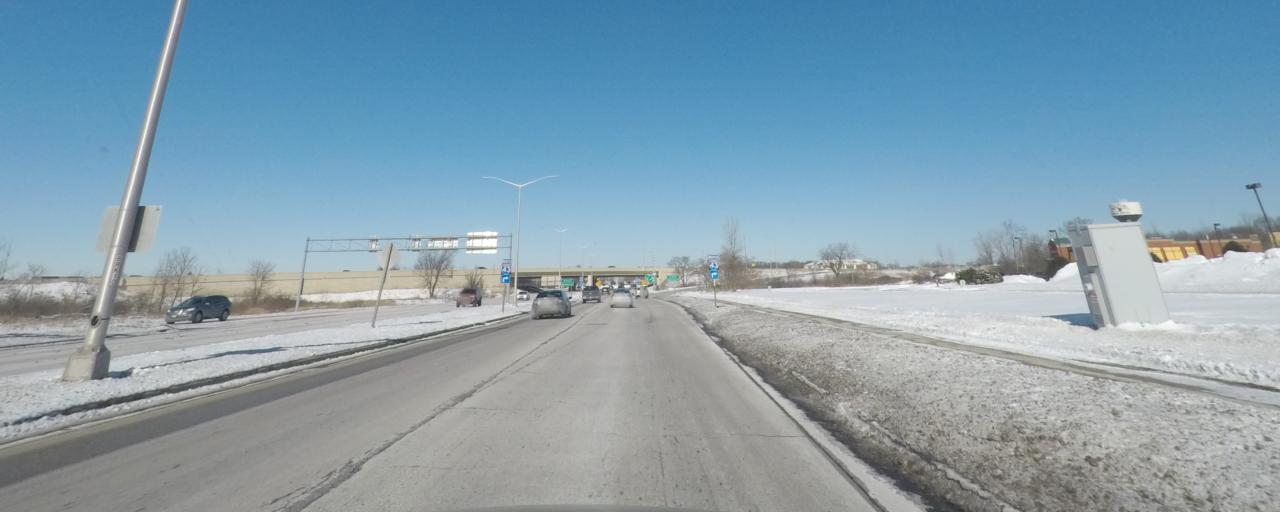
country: US
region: Wisconsin
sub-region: Waukesha County
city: New Berlin
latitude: 42.9498
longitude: -88.1088
